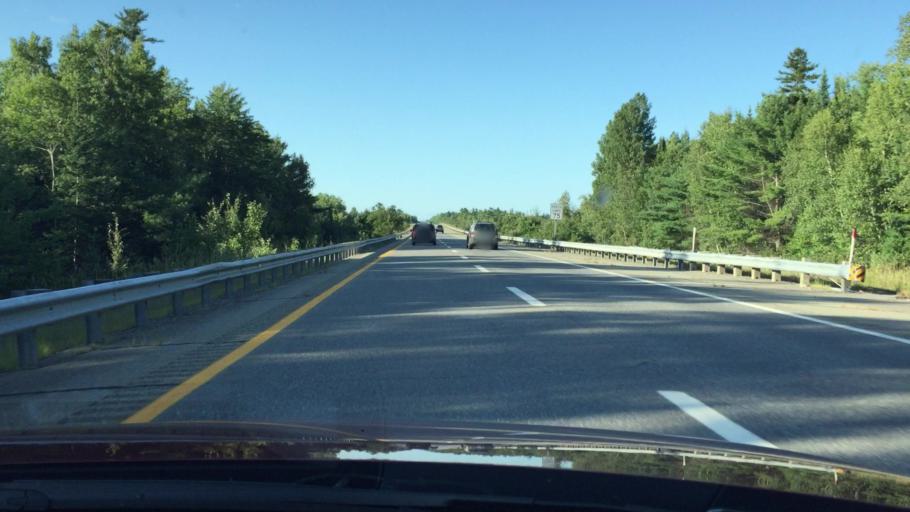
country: US
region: Maine
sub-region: Penobscot County
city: Lincoln
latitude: 45.3907
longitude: -68.6023
